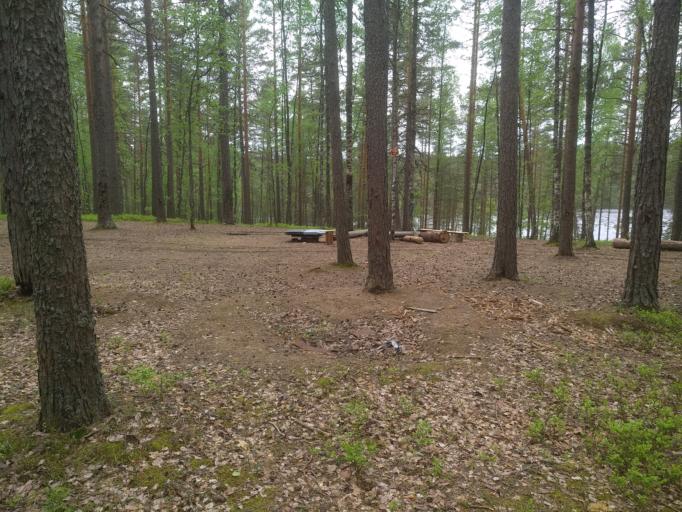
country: RU
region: Leningrad
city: Michurinskoye
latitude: 60.5982
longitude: 29.9198
